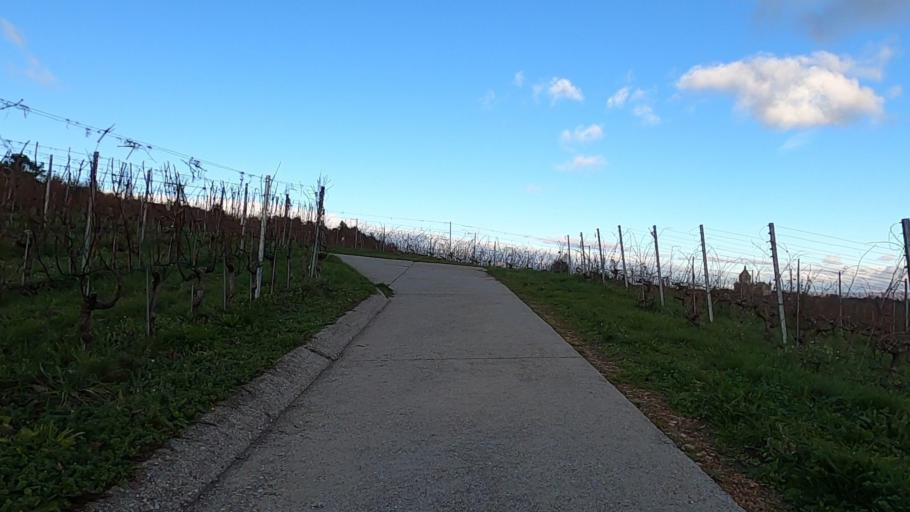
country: CH
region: Vaud
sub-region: Morges District
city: Morges
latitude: 46.5188
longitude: 6.4640
